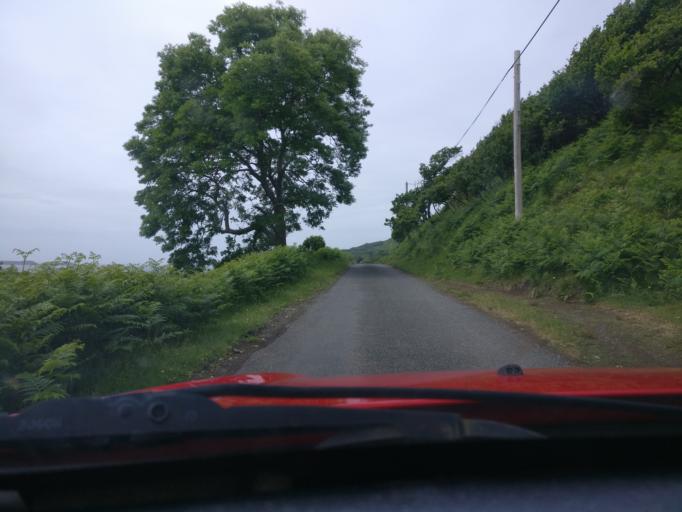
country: GB
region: Scotland
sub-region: Argyll and Bute
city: Isle Of Mull
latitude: 56.5311
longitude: -6.2293
